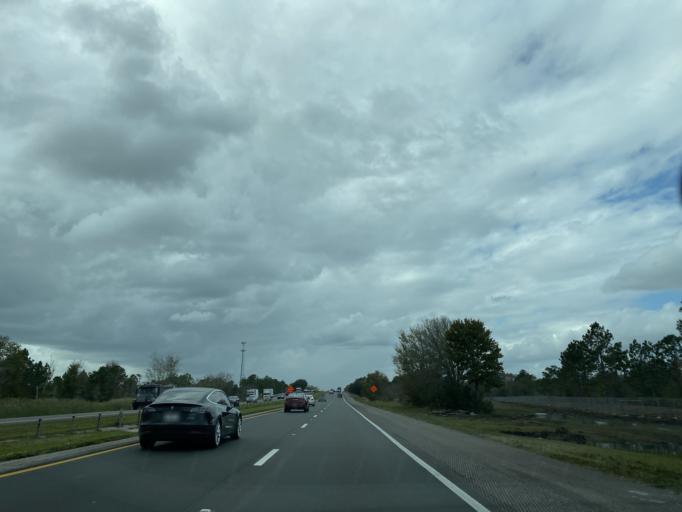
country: US
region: Florida
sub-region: Orange County
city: Wedgefield
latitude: 28.4520
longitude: -81.1369
